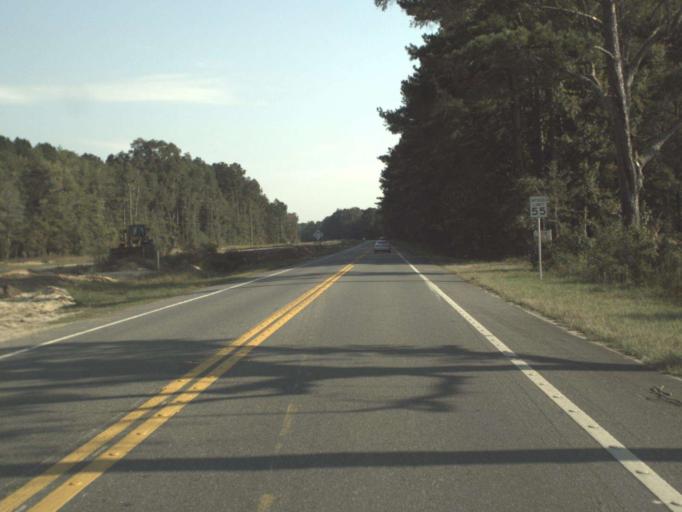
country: US
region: Florida
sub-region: Holmes County
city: Bonifay
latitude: 30.6364
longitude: -85.7063
